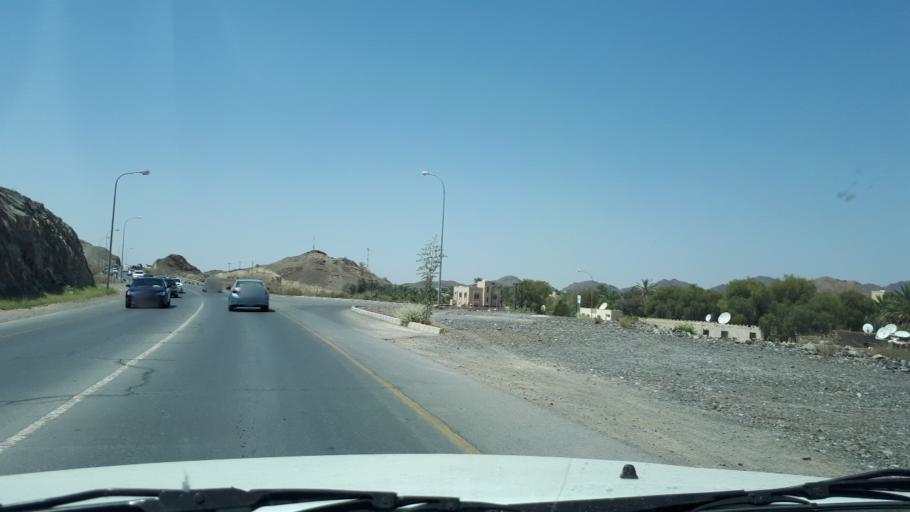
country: OM
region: Muhafazat ad Dakhiliyah
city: Bahla'
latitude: 22.9755
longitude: 57.3043
